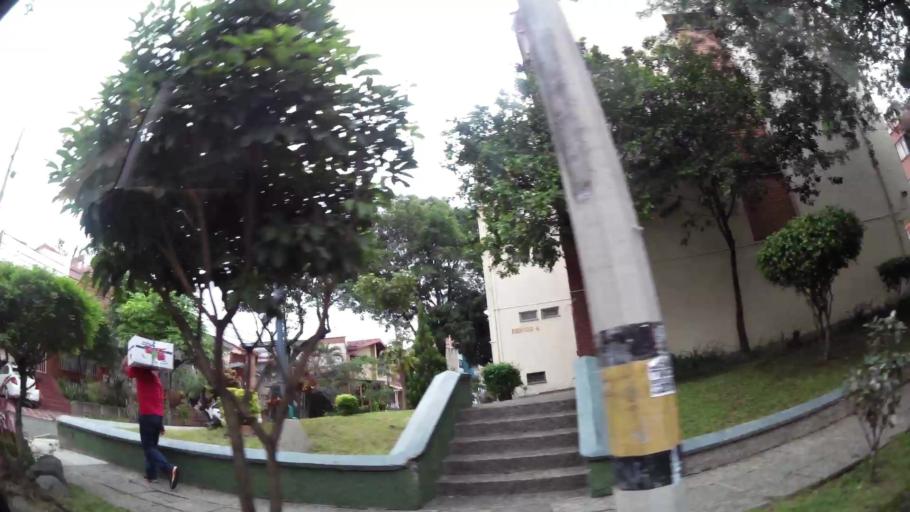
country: CO
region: Antioquia
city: Medellin
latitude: 6.2670
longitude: -75.5924
